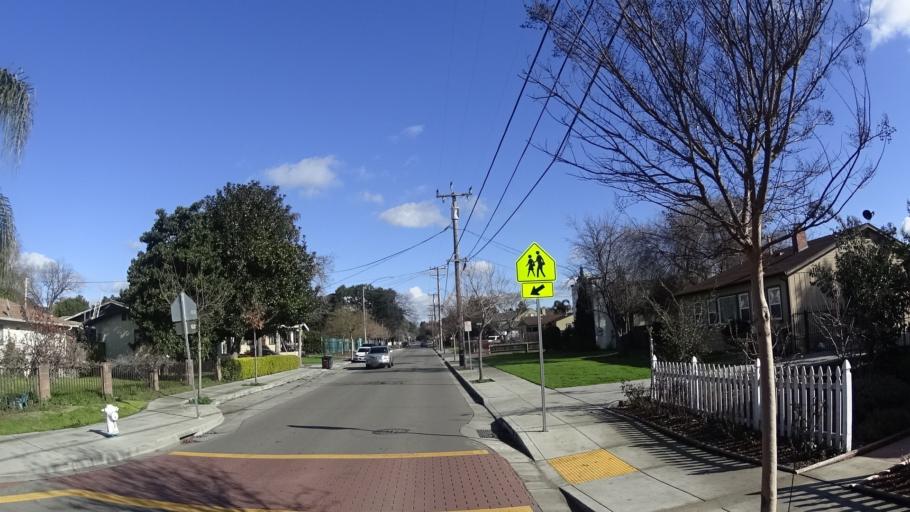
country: US
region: California
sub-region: Alameda County
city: San Lorenzo
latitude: 37.6837
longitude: -122.1150
